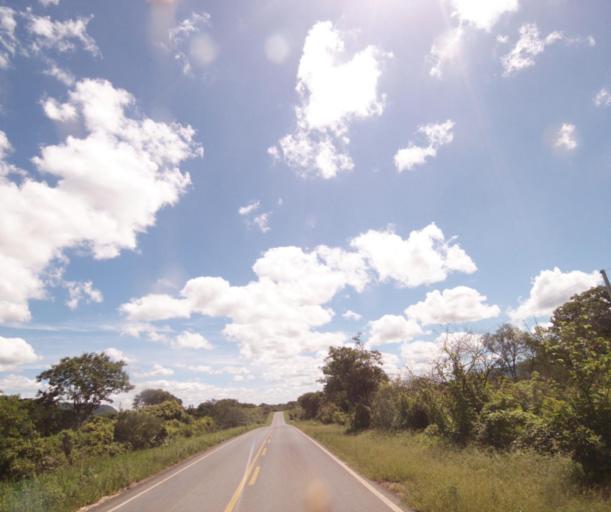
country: BR
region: Bahia
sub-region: Sao Felix Do Coribe
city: Santa Maria da Vitoria
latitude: -13.4006
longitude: -44.1458
